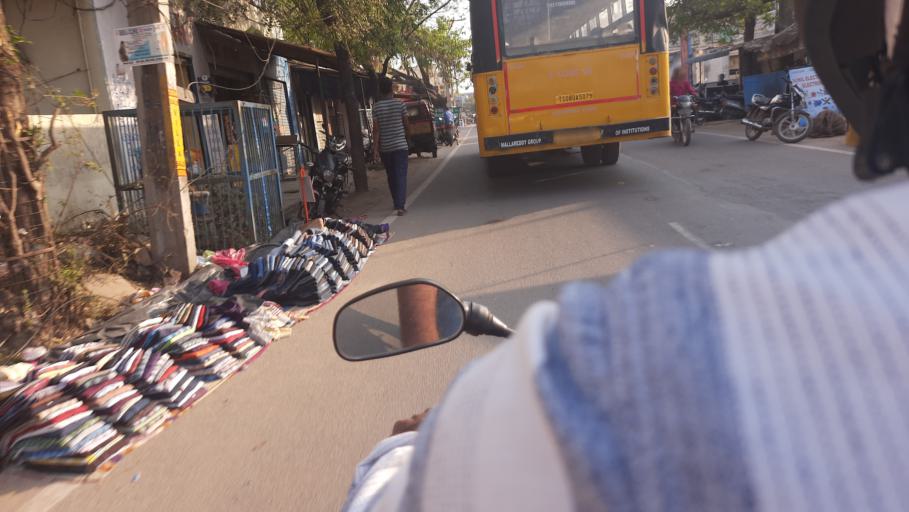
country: IN
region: Telangana
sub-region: Rangareddi
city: Secunderabad
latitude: 17.5079
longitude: 78.5410
